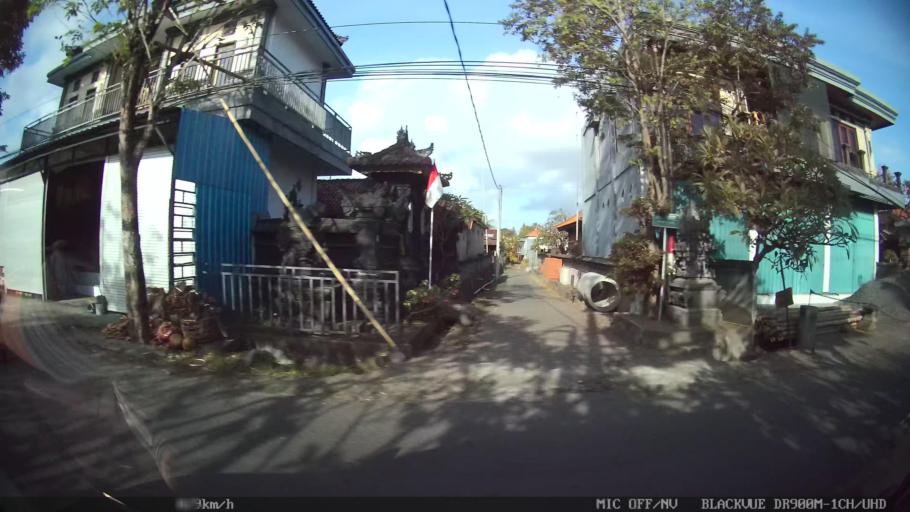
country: ID
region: Bali
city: Banjar Sedang
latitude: -8.5697
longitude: 115.2373
